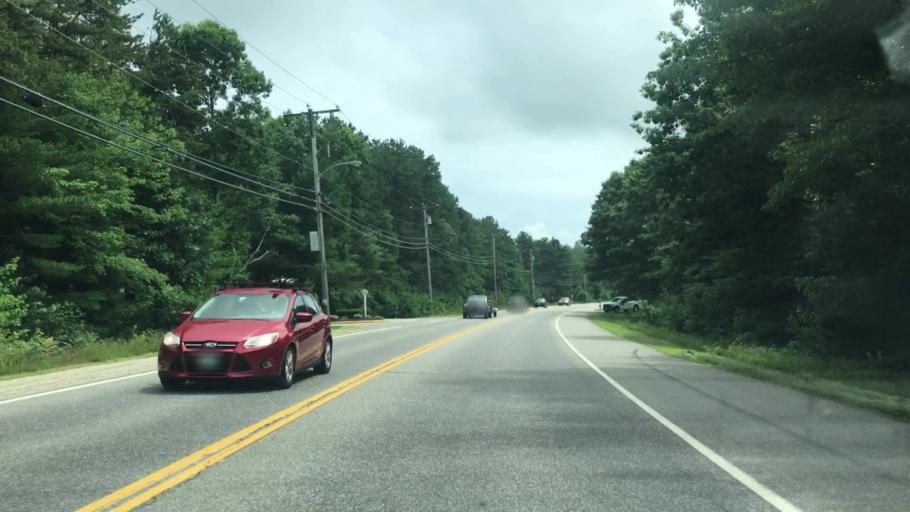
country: US
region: Maine
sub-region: Cumberland County
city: Brunswick
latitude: 43.8973
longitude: -69.9076
